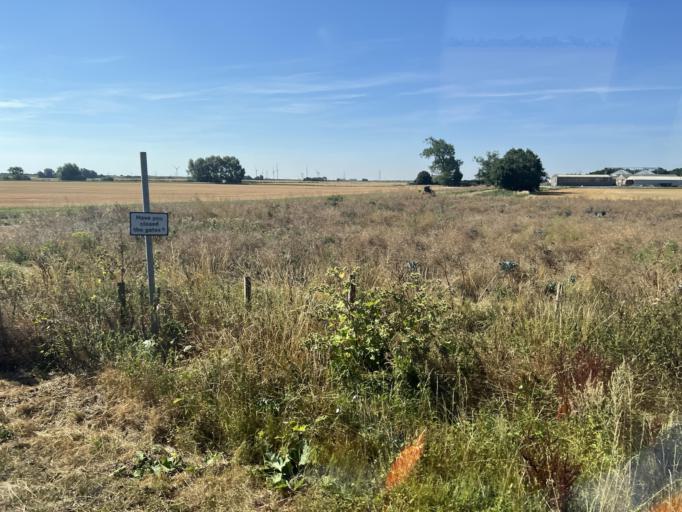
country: GB
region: England
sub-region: Lincolnshire
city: Donington
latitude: 52.9664
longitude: -0.2323
